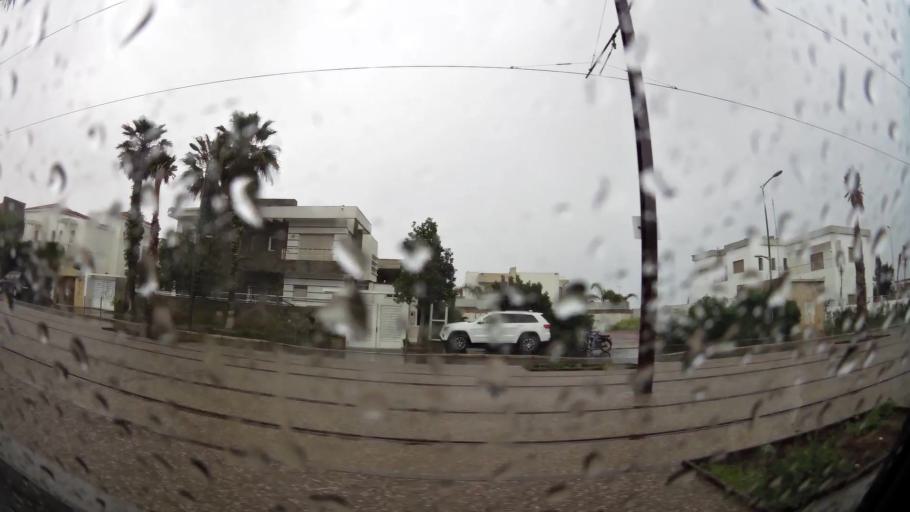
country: MA
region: Grand Casablanca
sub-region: Casablanca
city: Casablanca
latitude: 33.5429
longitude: -7.6638
